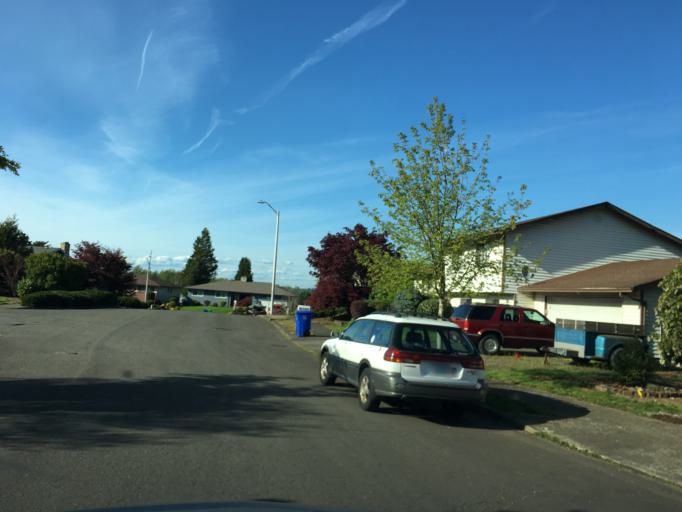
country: US
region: Oregon
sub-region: Multnomah County
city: Fairview
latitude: 45.5508
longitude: -122.5133
